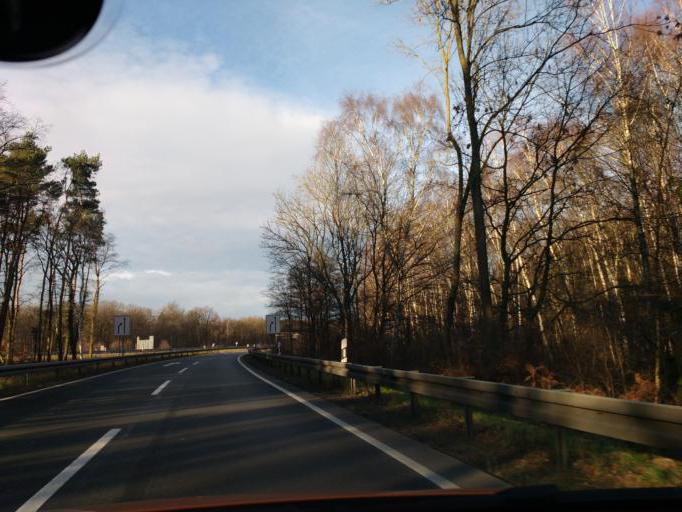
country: DE
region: Lower Saxony
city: Lehrte
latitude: 52.3989
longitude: 9.9014
